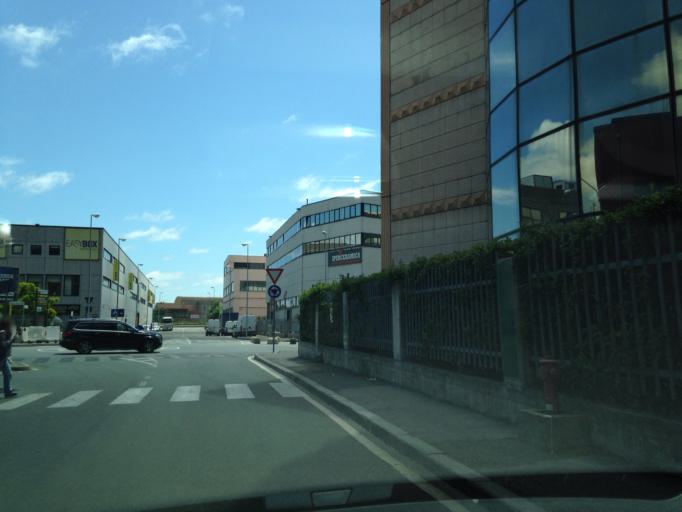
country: IT
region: Liguria
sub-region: Provincia di Genova
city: San Teodoro
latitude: 44.4211
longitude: 8.8807
